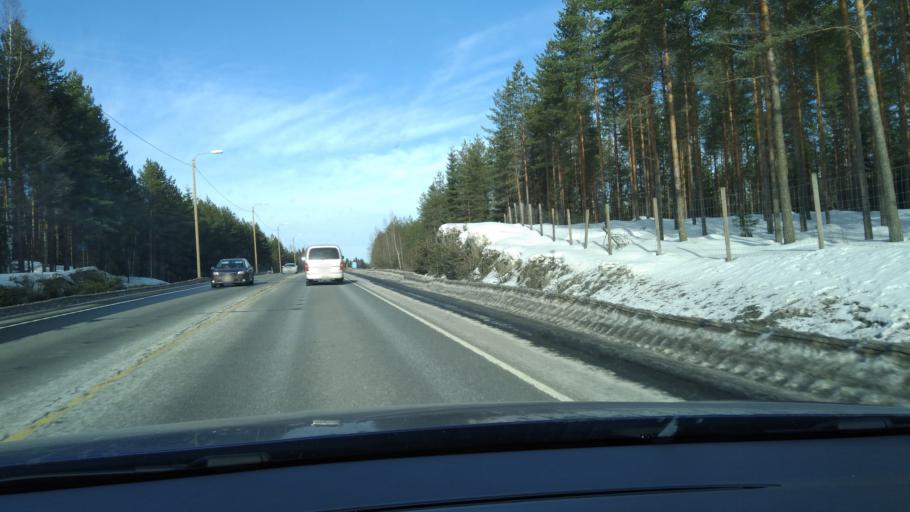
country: FI
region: Pirkanmaa
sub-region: Tampere
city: Orivesi
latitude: 61.6650
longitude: 24.2691
